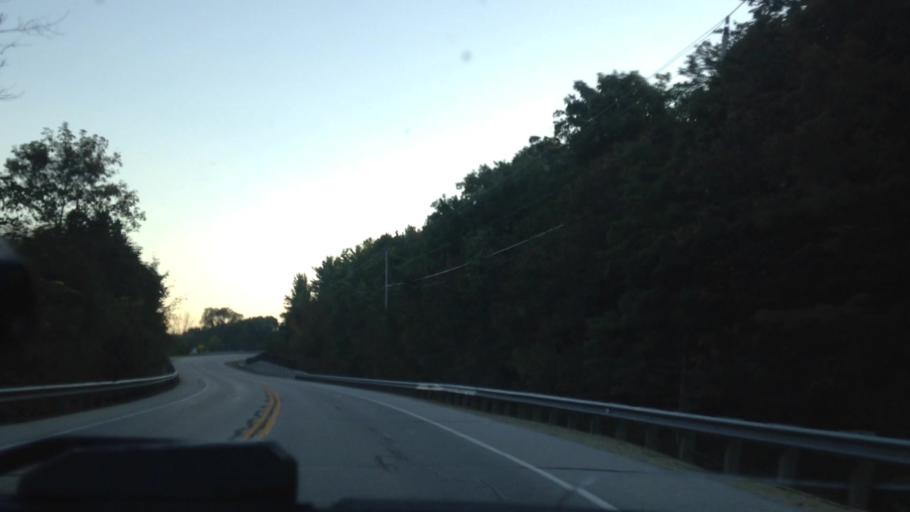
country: US
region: Wisconsin
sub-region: Washington County
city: Newburg
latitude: 43.4244
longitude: -88.0605
